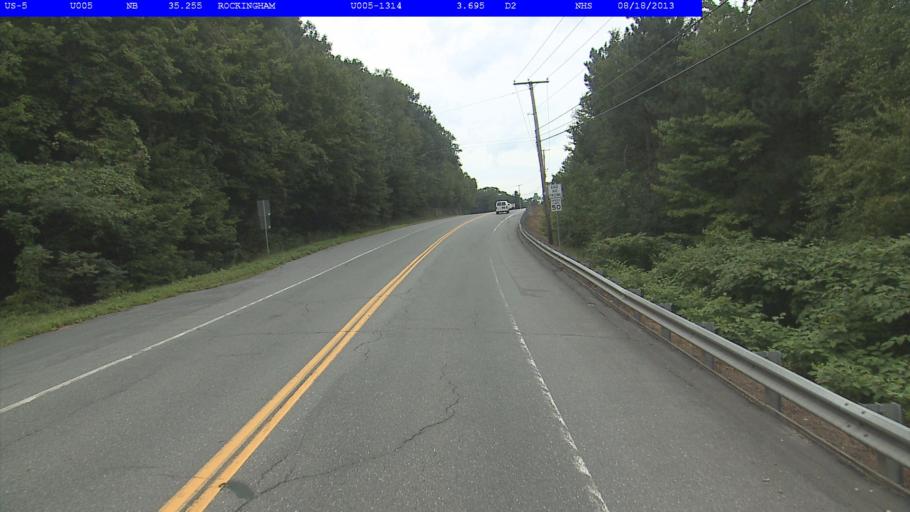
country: US
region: Vermont
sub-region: Windham County
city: Rockingham
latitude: 43.1743
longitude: -72.4591
